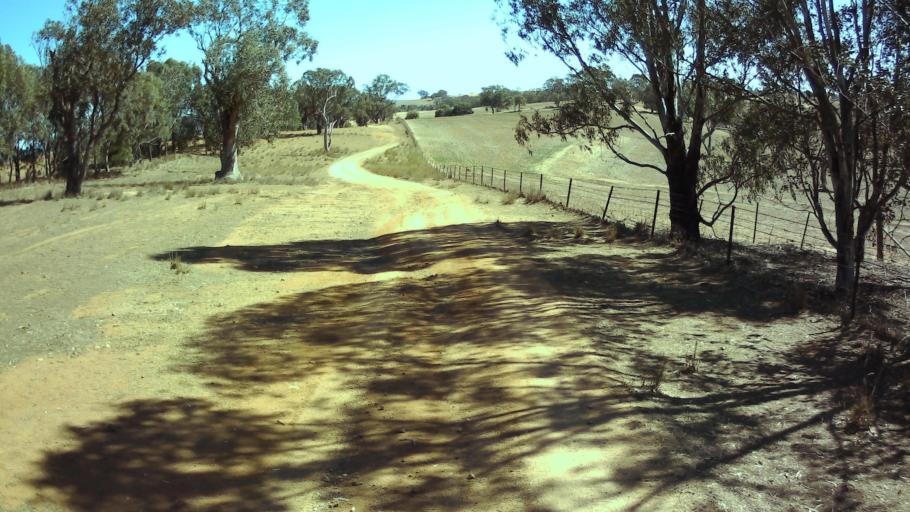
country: AU
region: New South Wales
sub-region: Weddin
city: Grenfell
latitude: -33.9947
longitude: 148.4365
